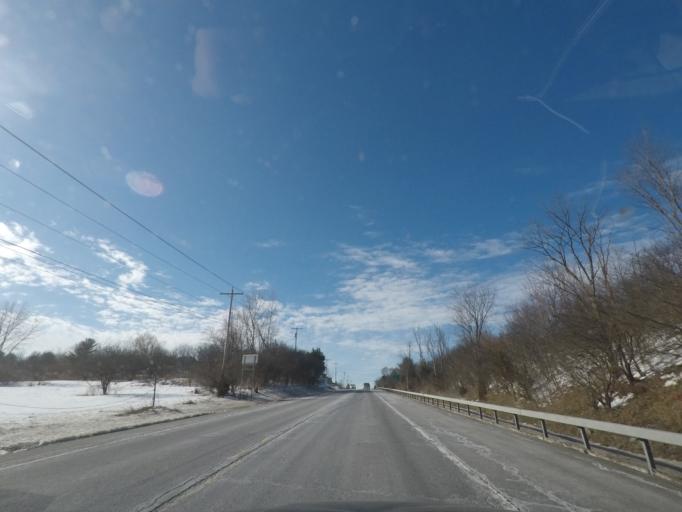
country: US
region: New York
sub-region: Albany County
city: Altamont
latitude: 42.7470
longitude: -74.0372
